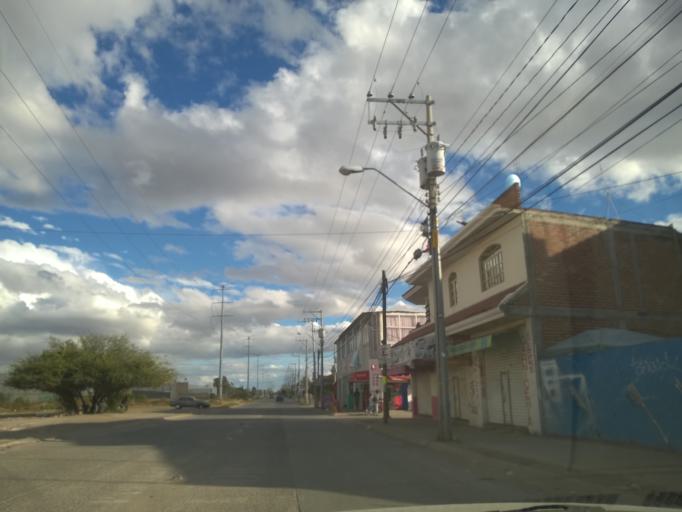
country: MX
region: Guanajuato
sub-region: Leon
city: Fraccionamiento Paraiso Real
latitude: 21.0741
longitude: -101.6145
